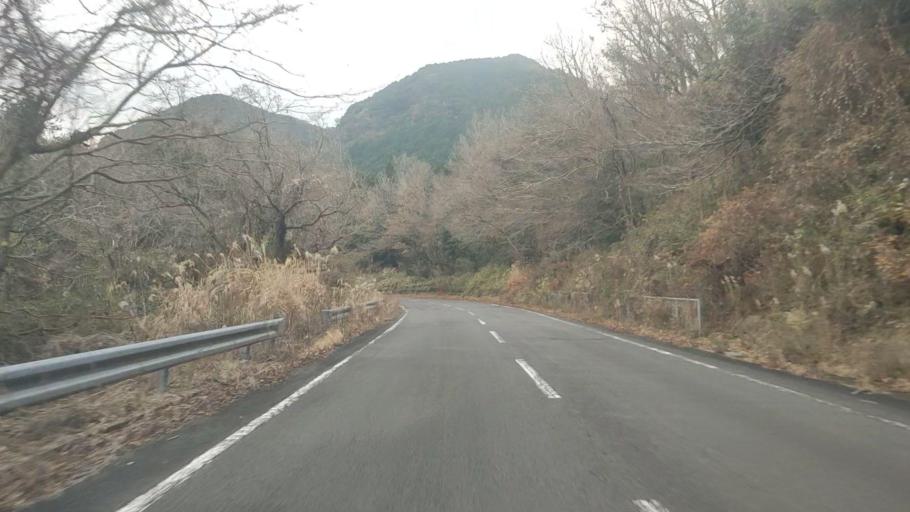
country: JP
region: Nagasaki
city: Shimabara
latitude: 32.7935
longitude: 130.2816
